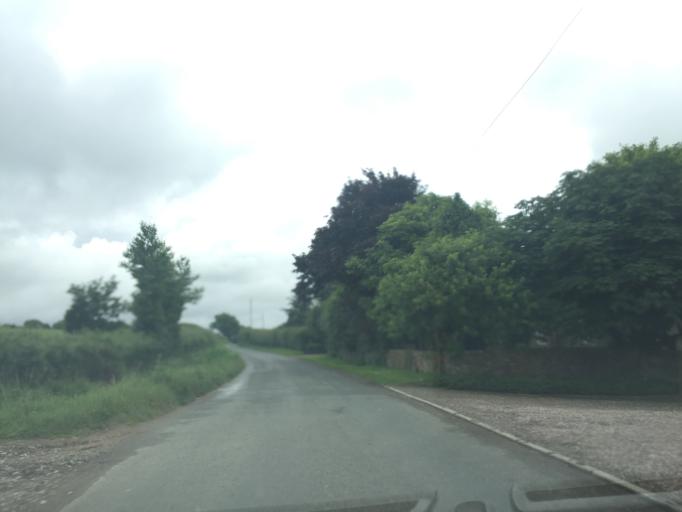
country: GB
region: England
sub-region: Dorset
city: Bovington Camp
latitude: 50.7197
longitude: -2.2995
